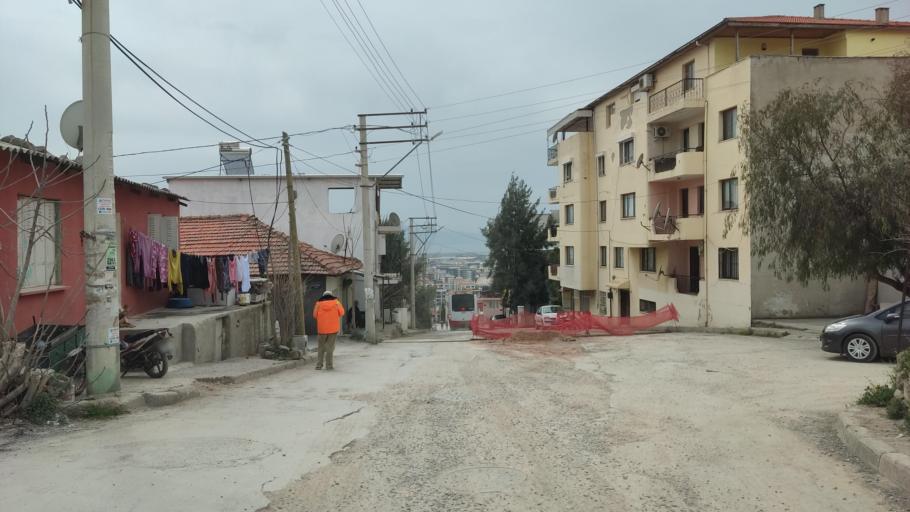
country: TR
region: Izmir
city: Karsiyaka
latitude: 38.4941
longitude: 27.0688
